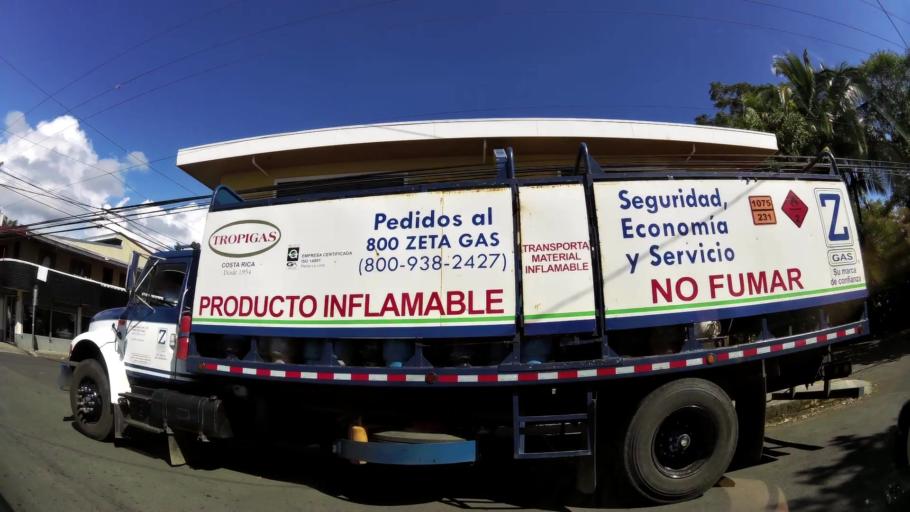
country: CR
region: Puntarenas
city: Quepos
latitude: 9.4323
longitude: -84.1637
